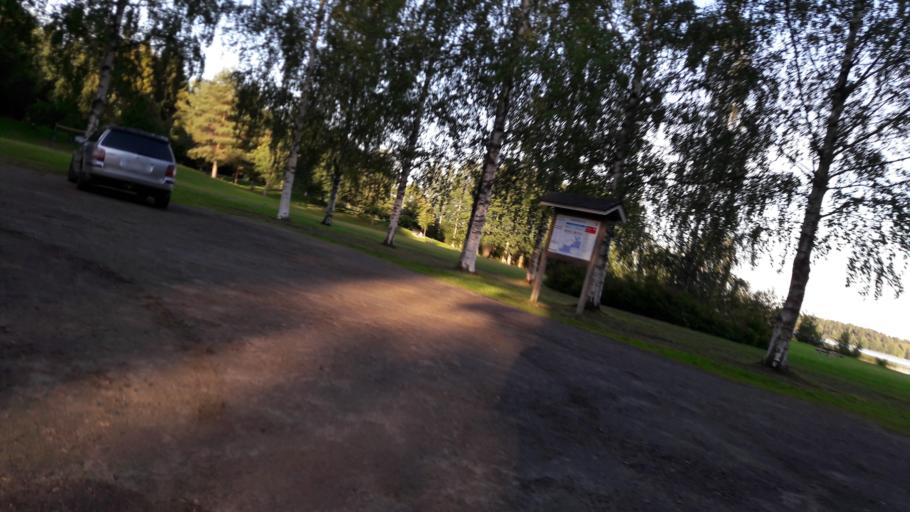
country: FI
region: North Karelia
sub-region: Joensuu
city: Joensuu
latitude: 62.6130
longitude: 29.6950
